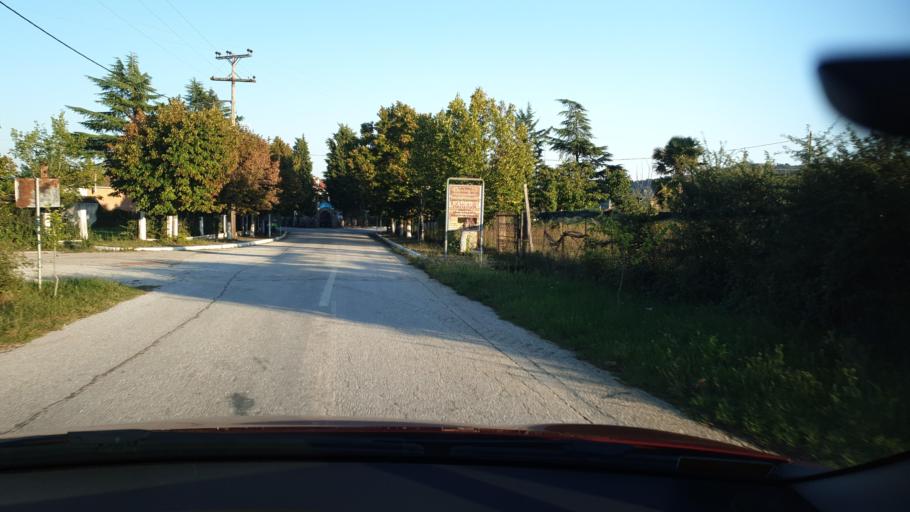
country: GR
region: Central Macedonia
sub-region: Nomos Chalkidikis
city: Galatista
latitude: 40.5190
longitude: 23.2830
